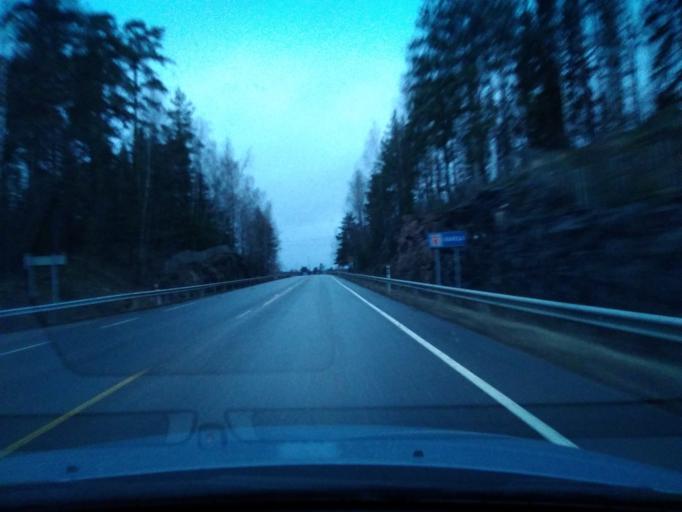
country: FI
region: Uusimaa
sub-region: Porvoo
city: Askola
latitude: 60.4909
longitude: 25.5560
